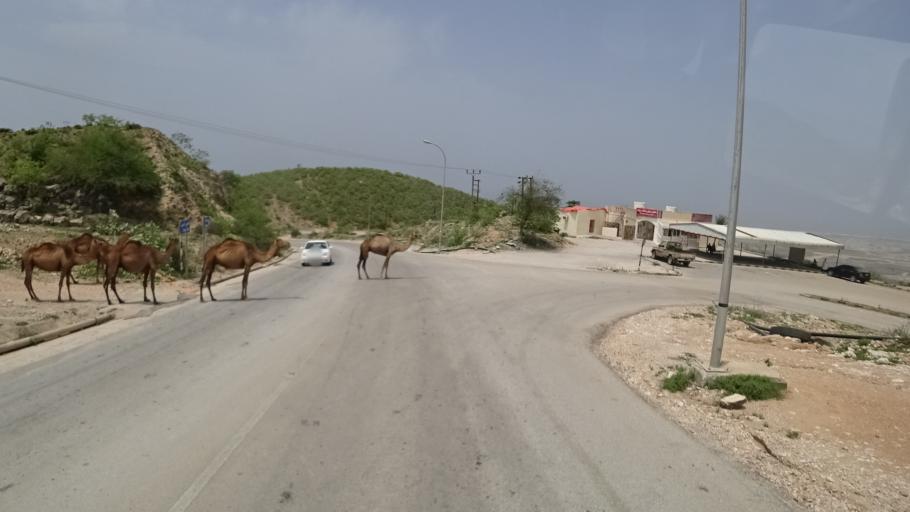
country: OM
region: Zufar
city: Salalah
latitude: 17.0705
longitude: 54.4467
